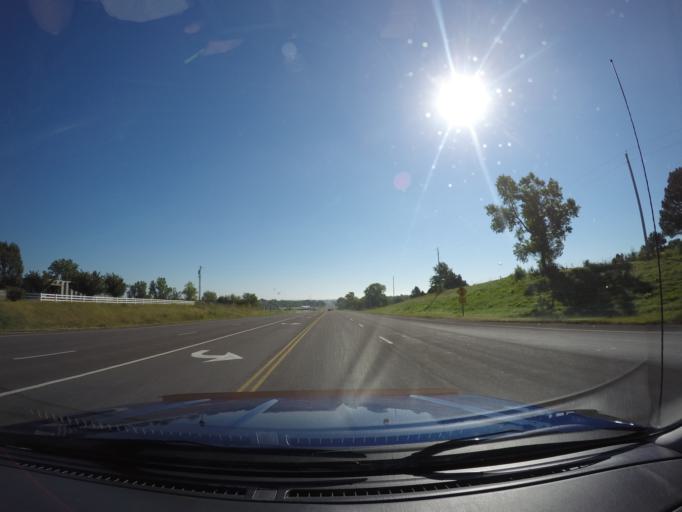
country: US
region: Kansas
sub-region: Pottawatomie County
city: Wamego
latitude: 39.2104
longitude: -96.3247
